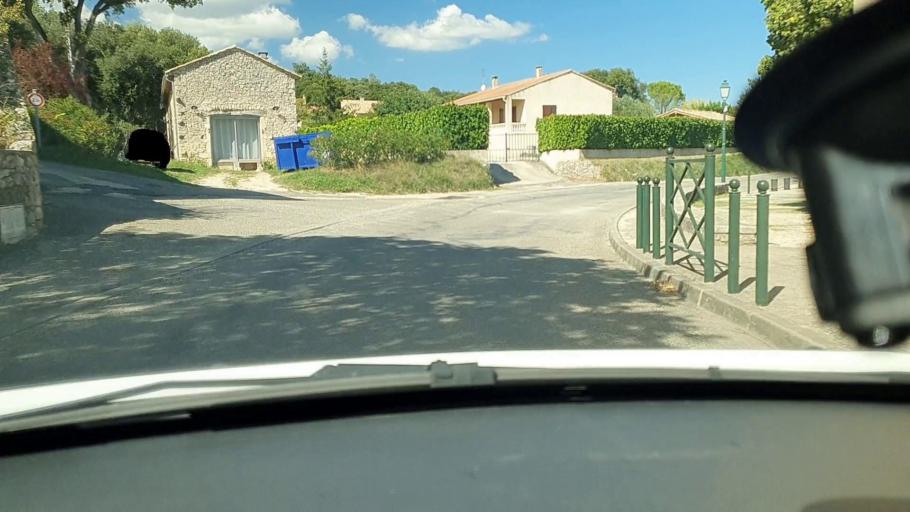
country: FR
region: Languedoc-Roussillon
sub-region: Departement du Gard
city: Goudargues
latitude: 44.1701
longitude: 4.4456
